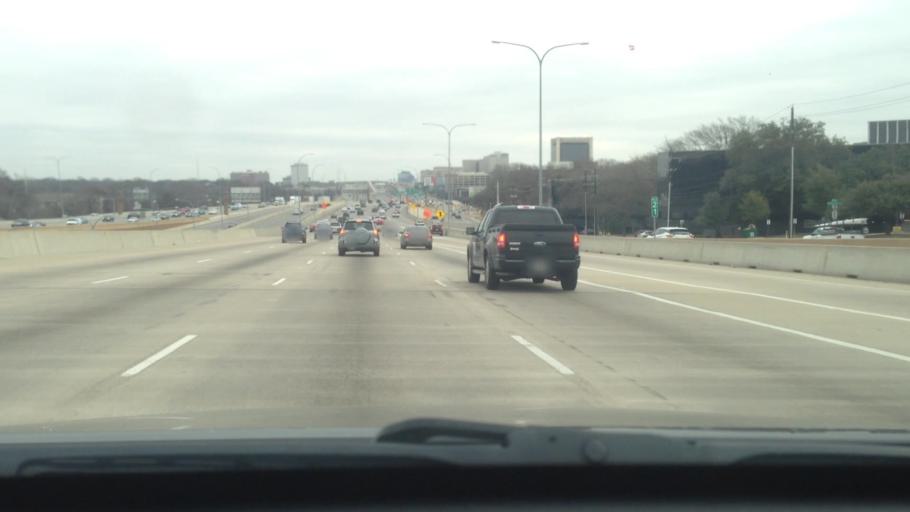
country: US
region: Texas
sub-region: Dallas County
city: Addison
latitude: 32.9247
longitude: -96.7911
